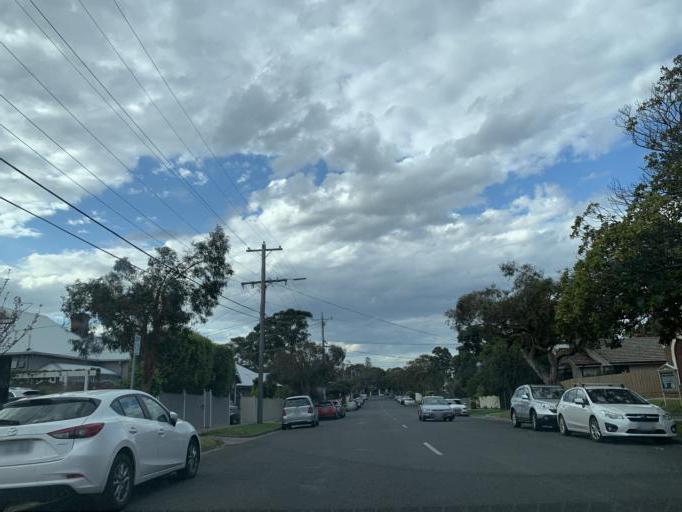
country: AU
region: Victoria
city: Hampton
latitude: -37.9512
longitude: 145.0059
